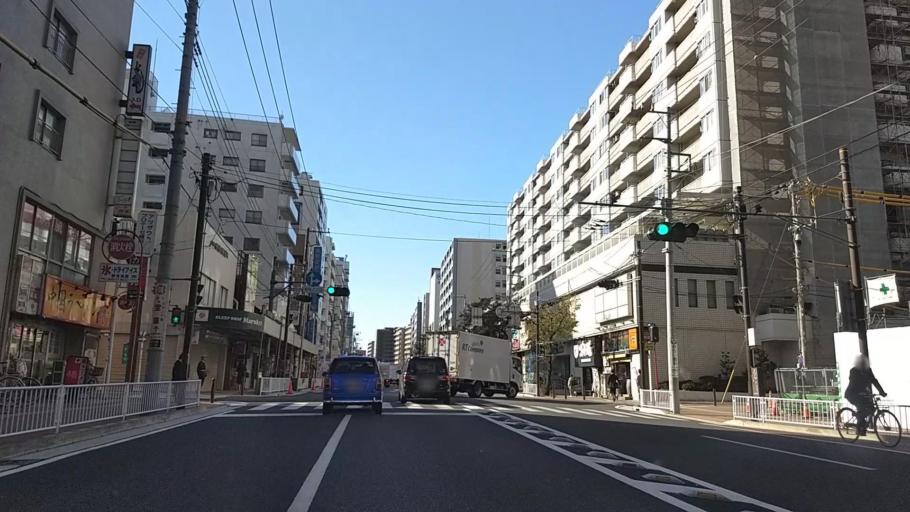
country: JP
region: Kanagawa
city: Yokohama
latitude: 35.4488
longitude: 139.6293
